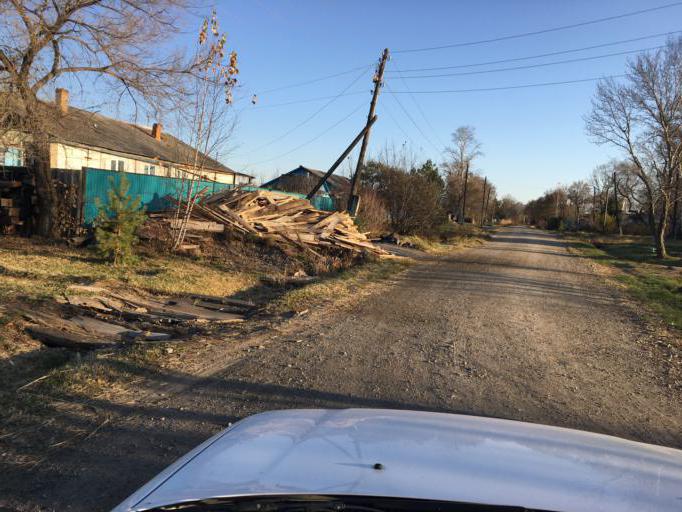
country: RU
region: Primorskiy
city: Lazo
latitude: 45.8644
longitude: 133.6396
